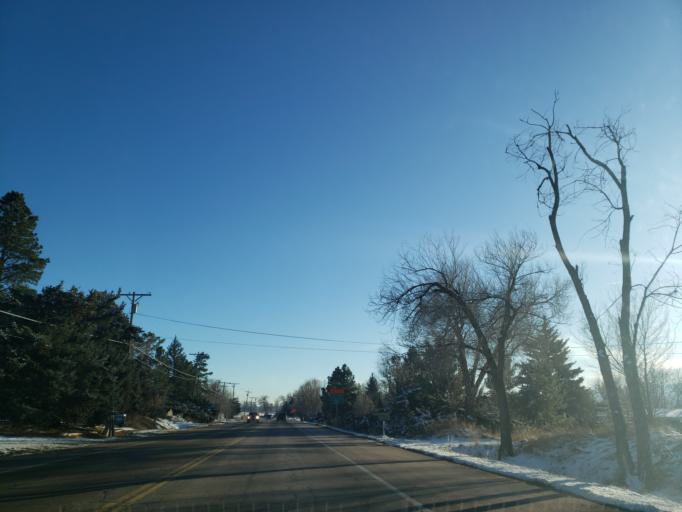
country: US
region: Colorado
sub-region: Larimer County
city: Fort Collins
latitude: 40.6243
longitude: -105.0716
